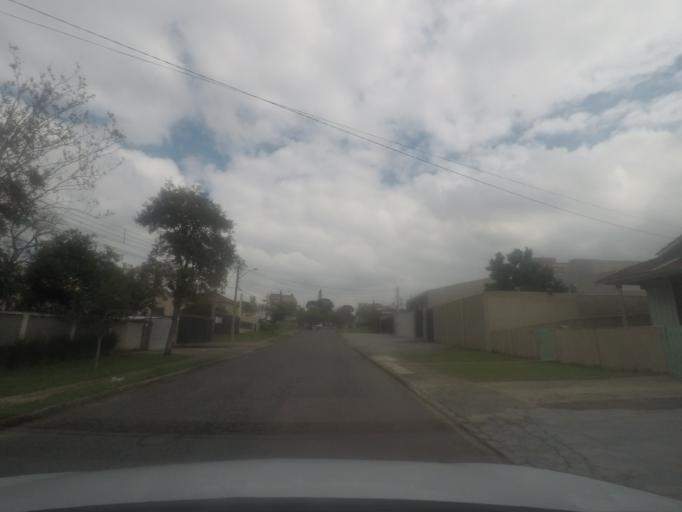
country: BR
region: Parana
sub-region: Curitiba
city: Curitiba
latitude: -25.4569
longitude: -49.2653
